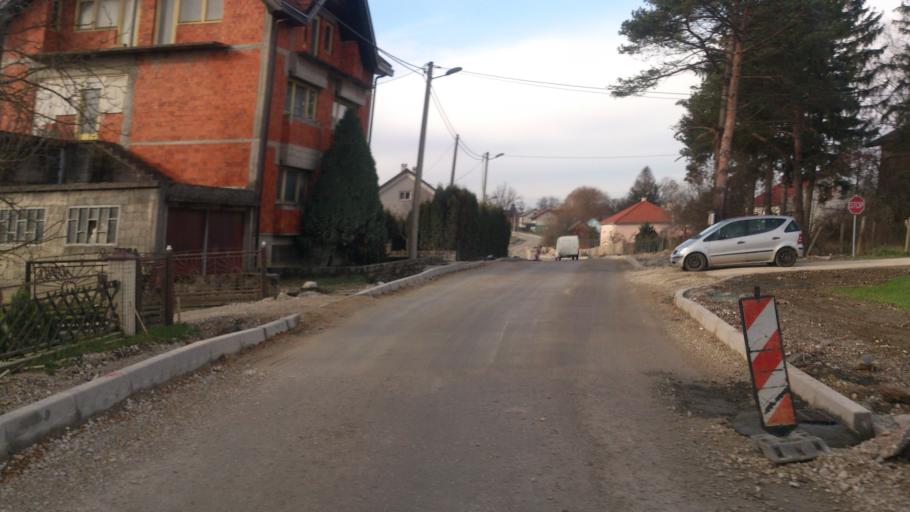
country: HR
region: Krapinsko-Zagorska
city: Marija Bistrica
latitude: 46.0495
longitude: 16.0989
